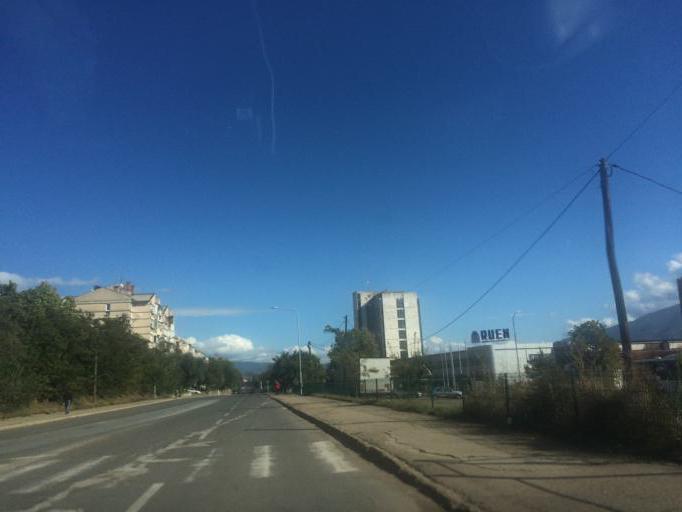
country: MK
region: Kocani
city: Kochani
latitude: 41.9143
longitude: 22.4247
